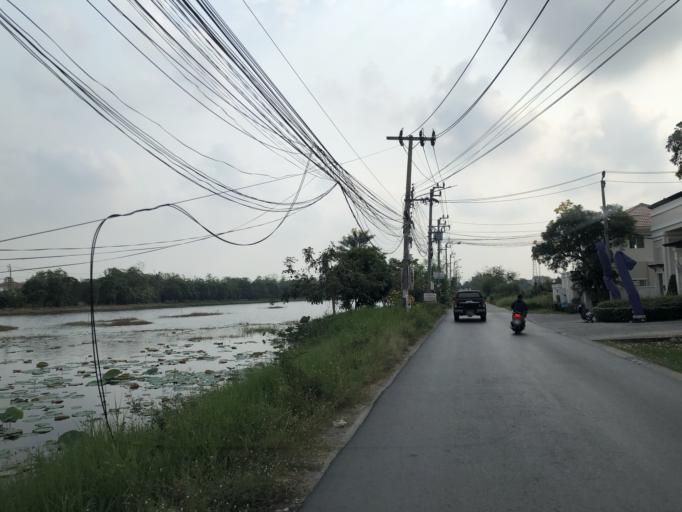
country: TH
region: Bangkok
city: Bang Na
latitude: 13.5854
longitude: 100.7039
